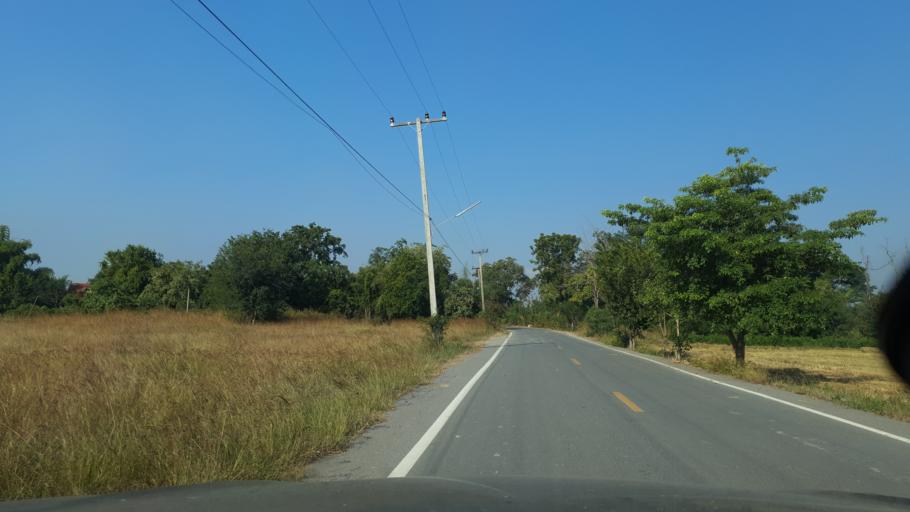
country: TH
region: Lamphun
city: Ban Thi
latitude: 18.6847
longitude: 99.1160
